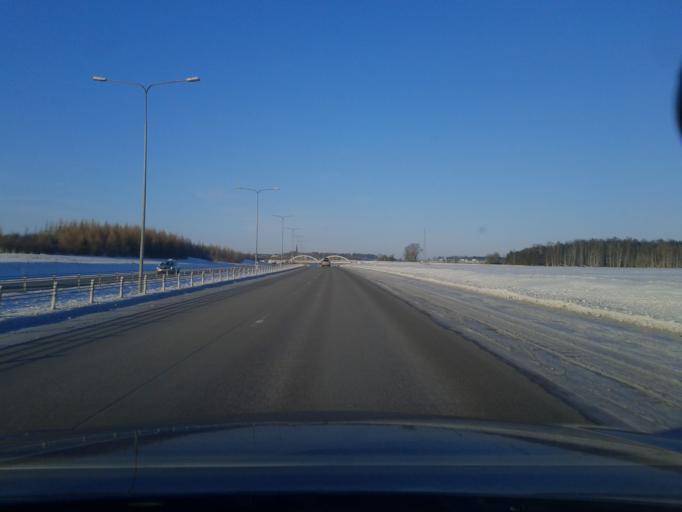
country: SE
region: Uppsala
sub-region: Uppsala Kommun
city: Saevja
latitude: 59.8630
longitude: 17.7208
